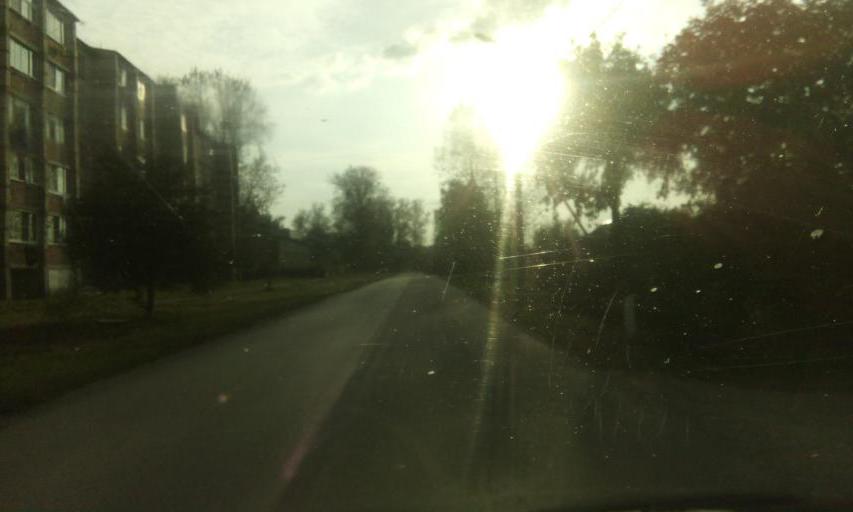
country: RU
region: Tula
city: Partizan
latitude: 53.9245
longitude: 38.0973
